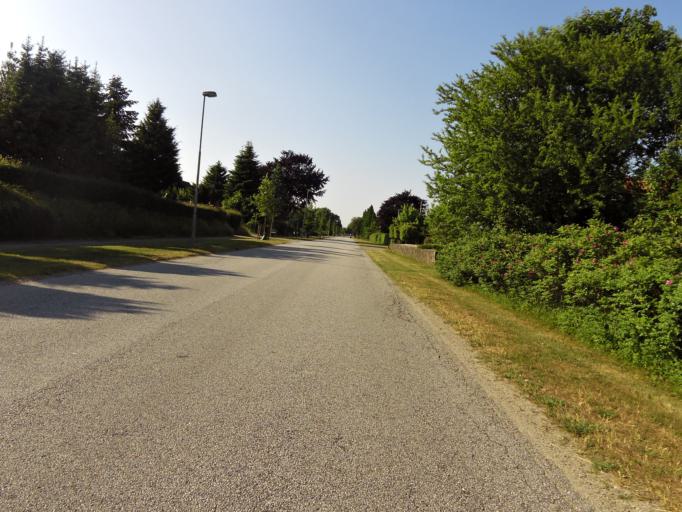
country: DK
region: South Denmark
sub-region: Haderslev Kommune
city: Vojens
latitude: 55.2387
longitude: 9.2955
